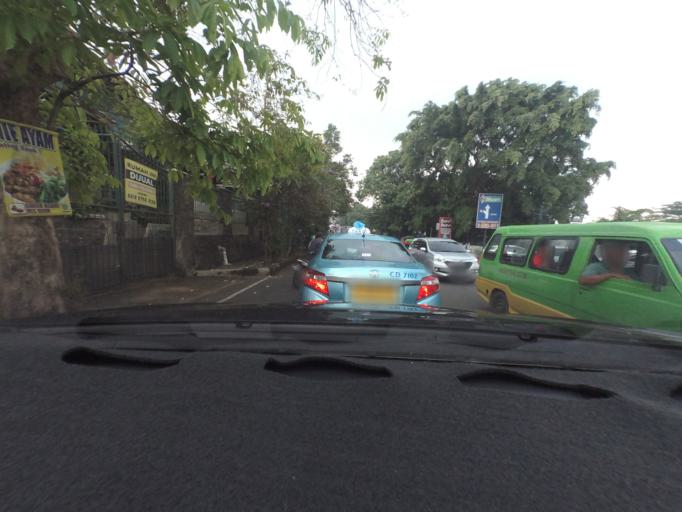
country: ID
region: West Java
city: Bogor
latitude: -6.5990
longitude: 106.8159
